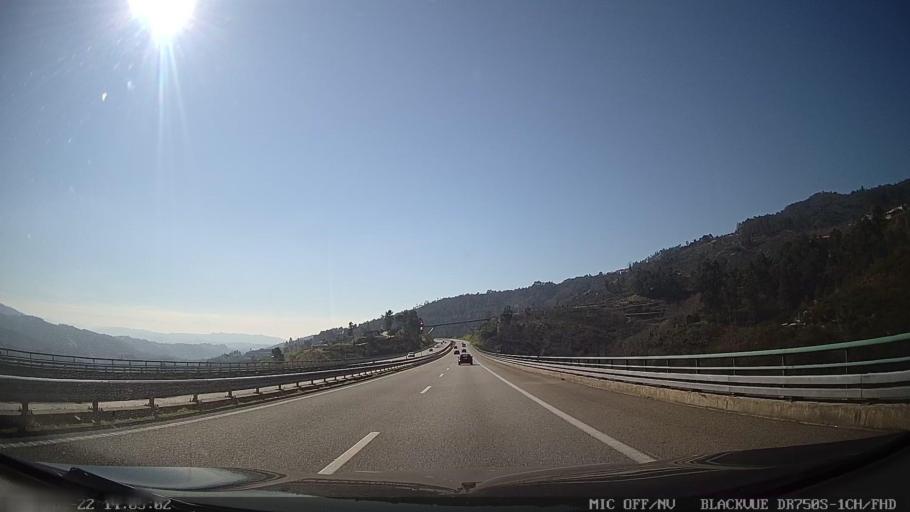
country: PT
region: Porto
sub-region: Amarante
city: Amarante
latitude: 41.2443
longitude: -8.1153
